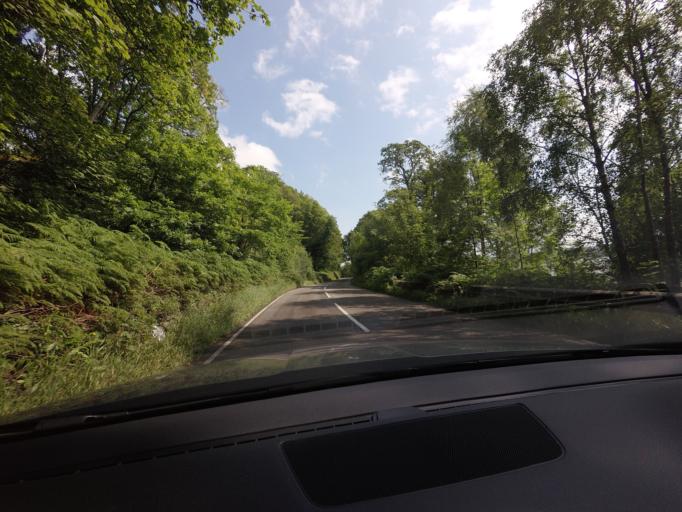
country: GB
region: Scotland
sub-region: Highland
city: Dingwall
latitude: 57.6170
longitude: -4.3945
